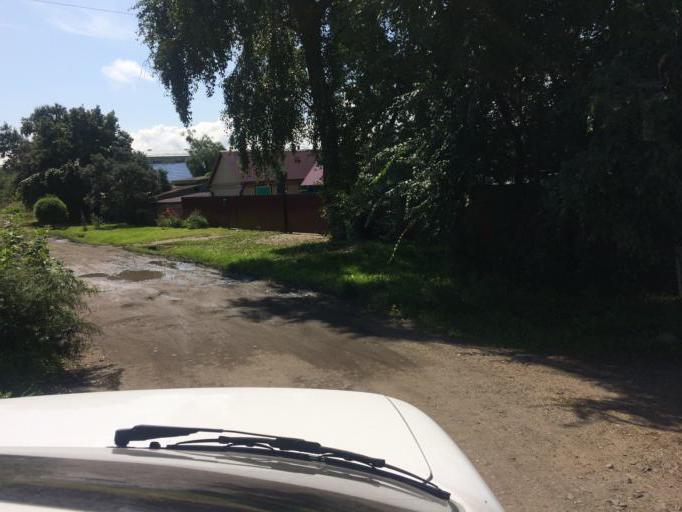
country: RU
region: Primorskiy
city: Dal'nerechensk
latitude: 45.9387
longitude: 133.7335
